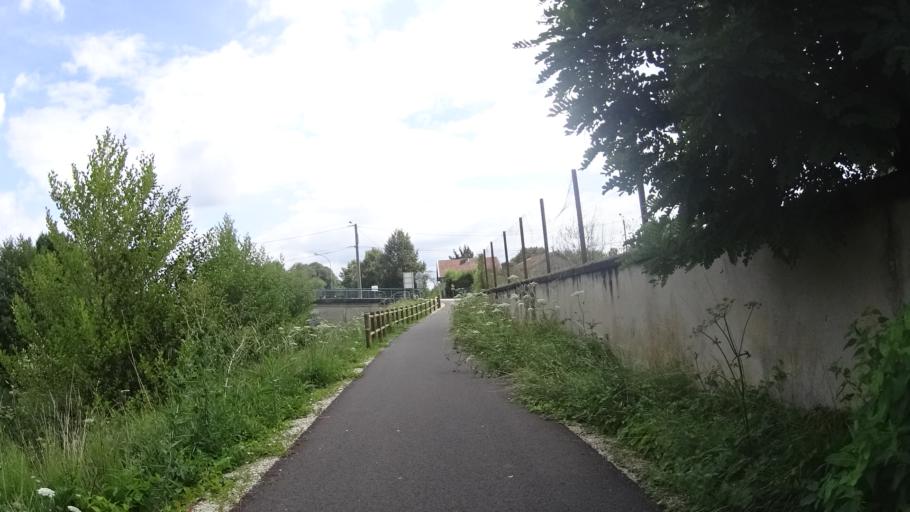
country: FR
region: Lorraine
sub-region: Departement de la Meuse
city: Commercy
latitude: 48.7700
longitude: 5.5823
